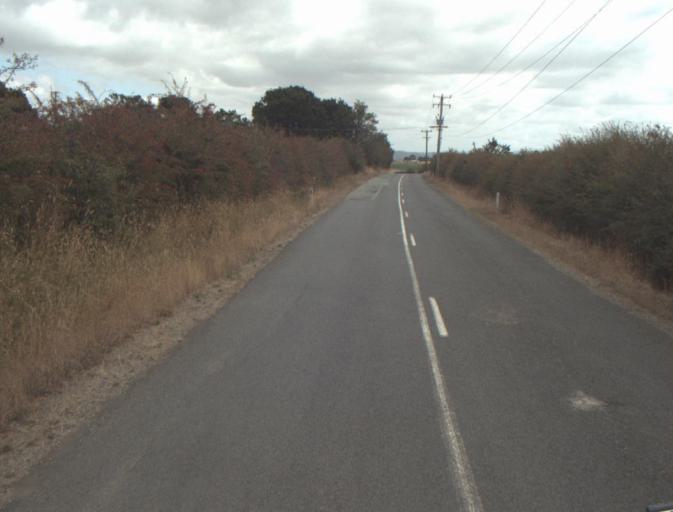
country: AU
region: Tasmania
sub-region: Northern Midlands
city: Evandale
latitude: -41.5055
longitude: 147.2639
